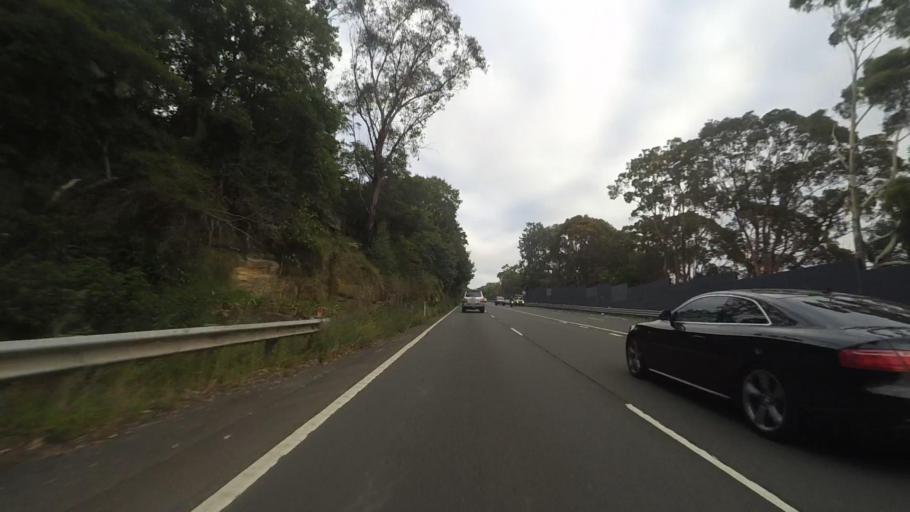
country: AU
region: New South Wales
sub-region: Sutherland Shire
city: Heathcote
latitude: -34.0751
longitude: 151.0070
